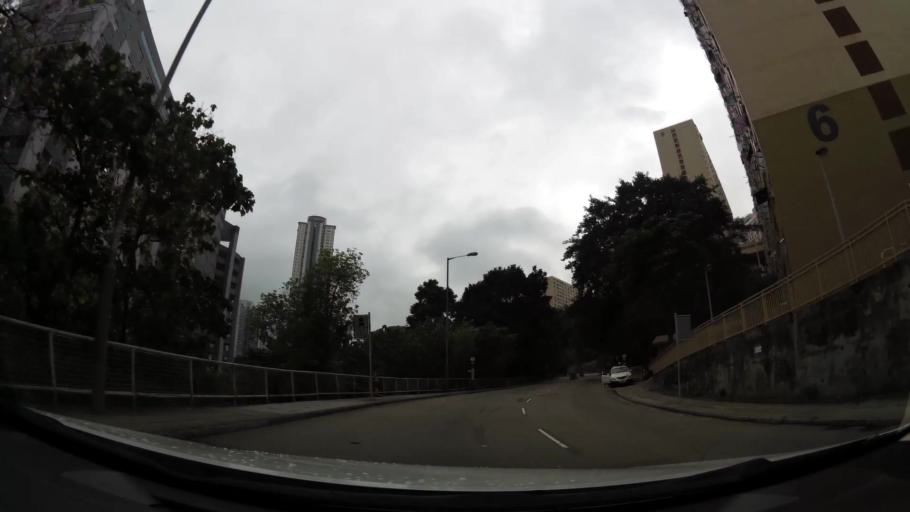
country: HK
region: Tsuen Wan
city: Tsuen Wan
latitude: 22.3618
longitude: 114.1209
